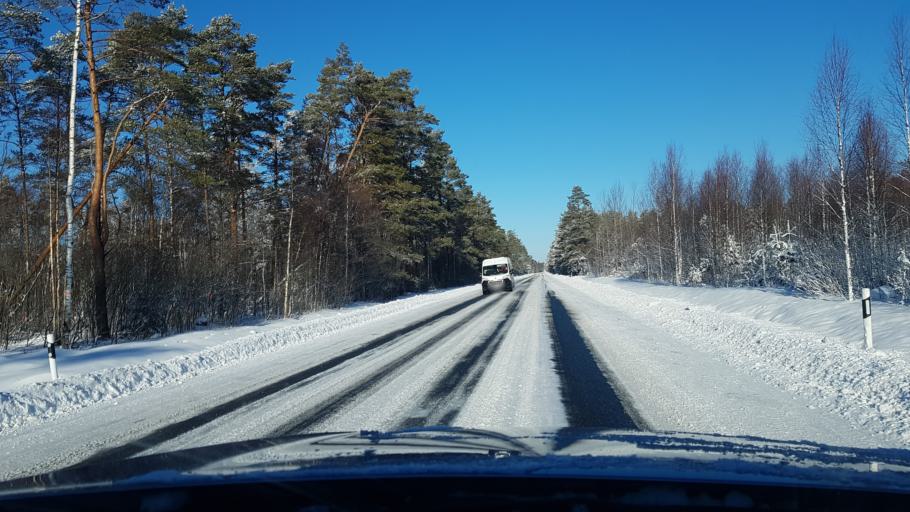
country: EE
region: Hiiumaa
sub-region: Kaerdla linn
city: Kardla
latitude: 58.9010
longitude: 22.7894
